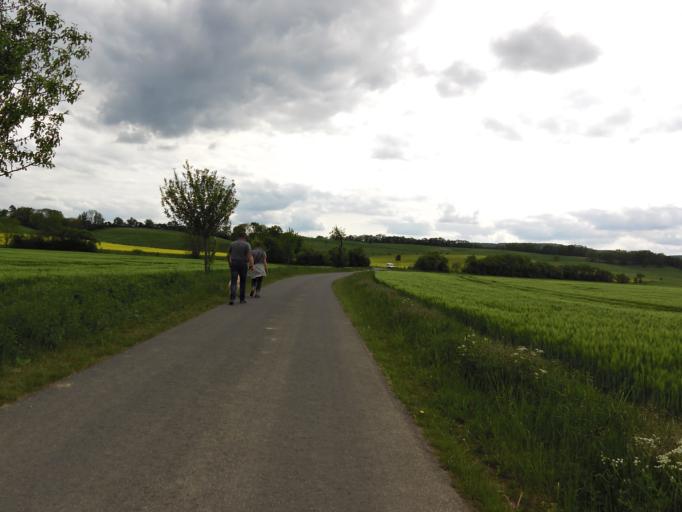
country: DE
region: Thuringia
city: Creuzburg
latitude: 51.0362
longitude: 10.2446
